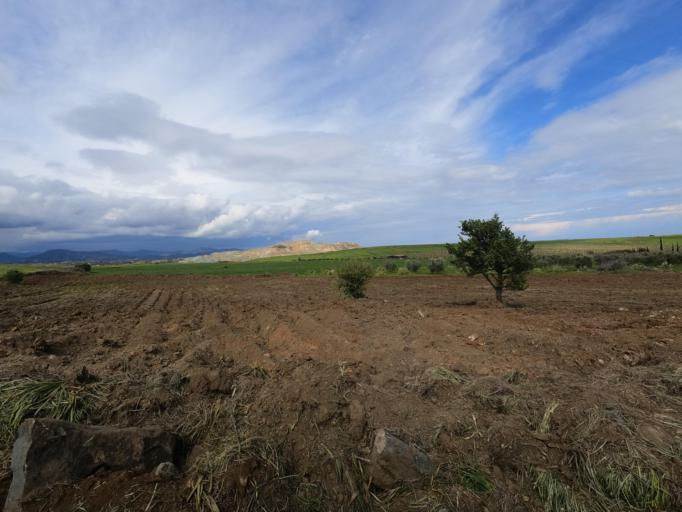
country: CY
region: Lefkosia
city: Lefka
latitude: 35.0870
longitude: 32.9277
